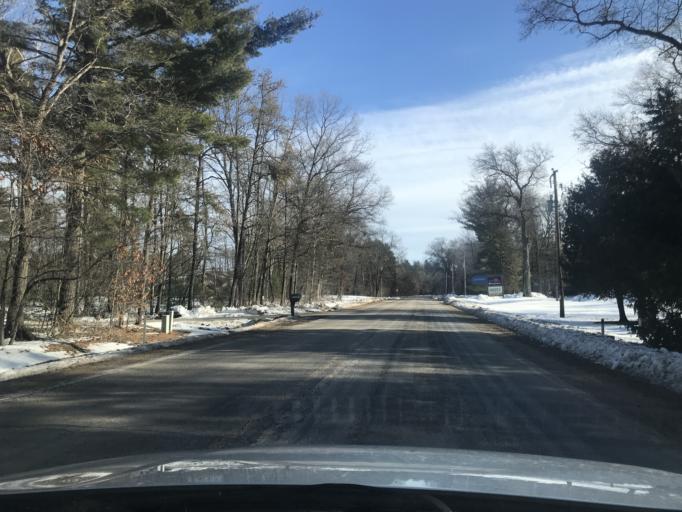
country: US
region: Wisconsin
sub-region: Marinette County
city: Peshtigo
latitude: 45.0304
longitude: -87.7105
